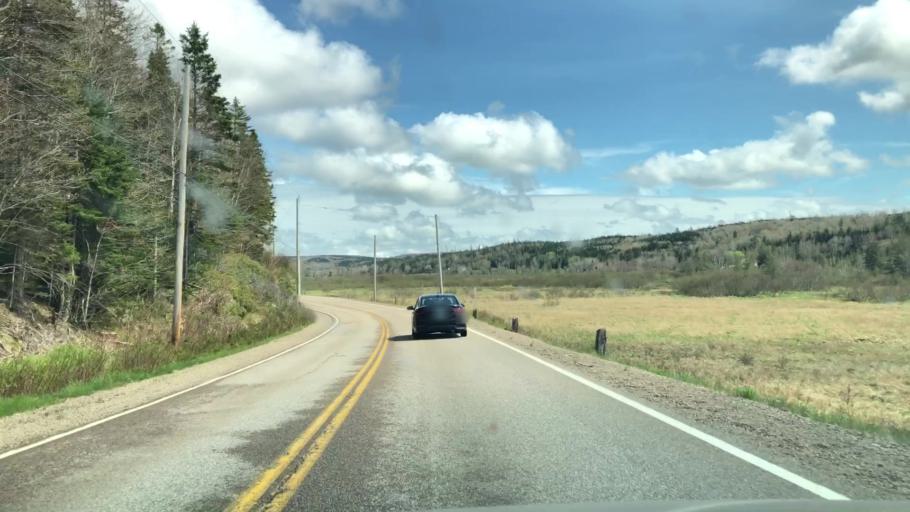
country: CA
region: Nova Scotia
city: Antigonish
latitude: 45.1966
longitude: -62.0015
